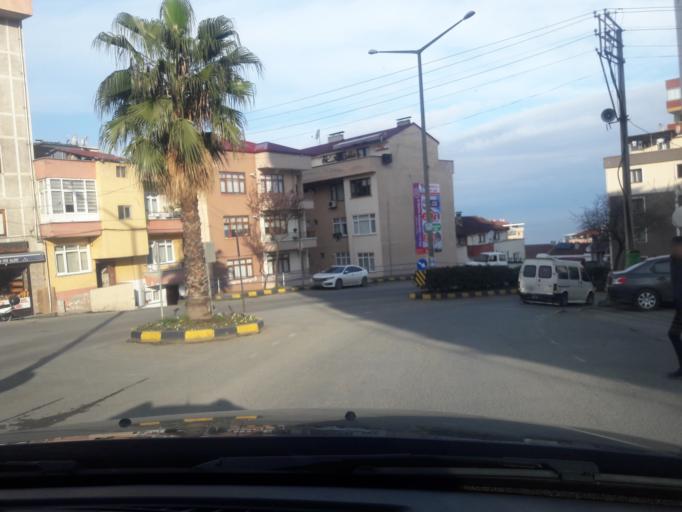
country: TR
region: Trabzon
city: Trabzon
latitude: 40.9963
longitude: 39.6915
